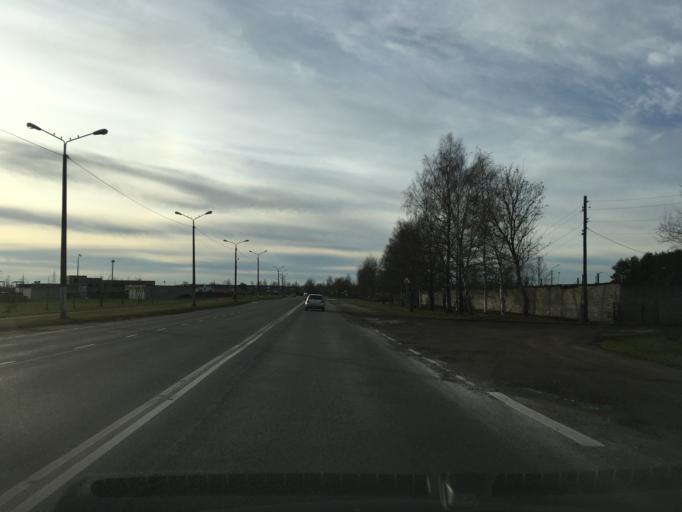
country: EE
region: Ida-Virumaa
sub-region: Narva linn
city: Narva
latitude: 59.3805
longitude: 28.1566
